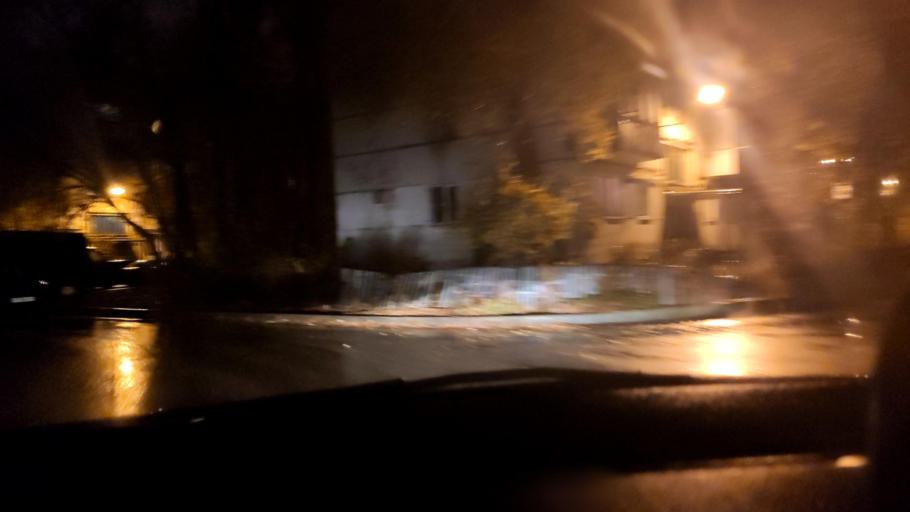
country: RU
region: Voronezj
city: Voronezh
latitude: 51.6478
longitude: 39.1415
